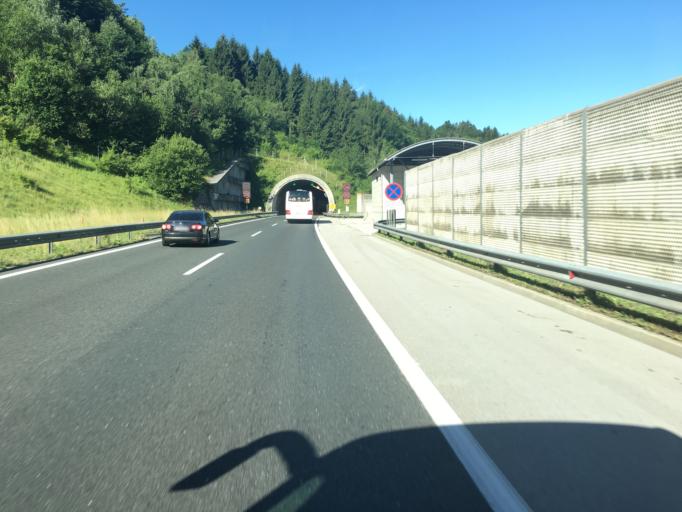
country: SI
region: Zagorje ob Savi
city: Izlake
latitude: 46.1901
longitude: 14.8970
